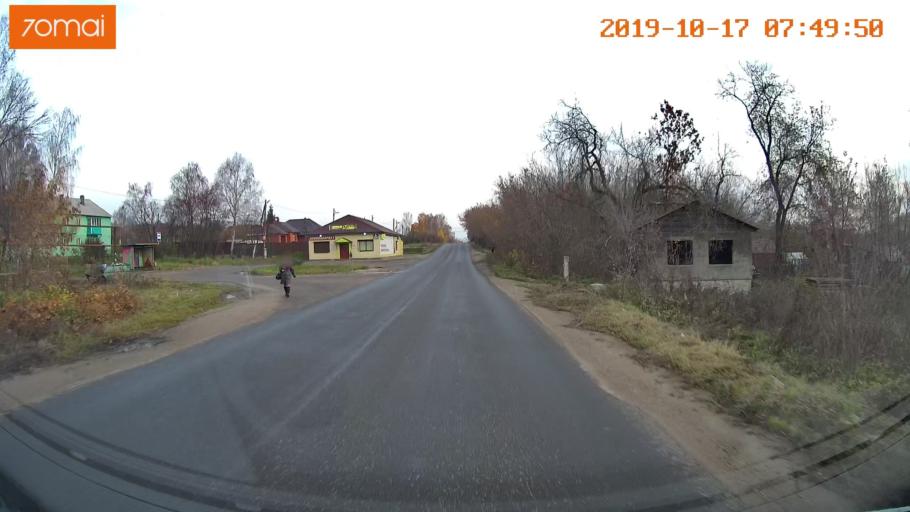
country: RU
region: Vladimir
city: Yur'yev-Pol'skiy
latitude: 56.4803
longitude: 39.6656
